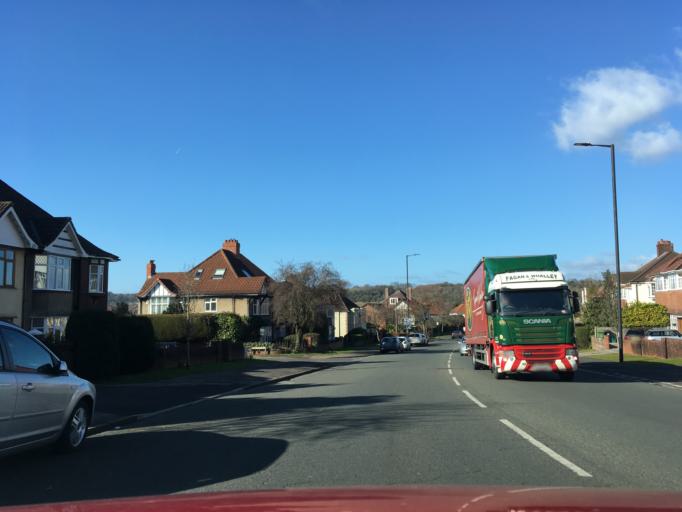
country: GB
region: England
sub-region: Bristol
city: Bristol
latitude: 51.4894
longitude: -2.6197
